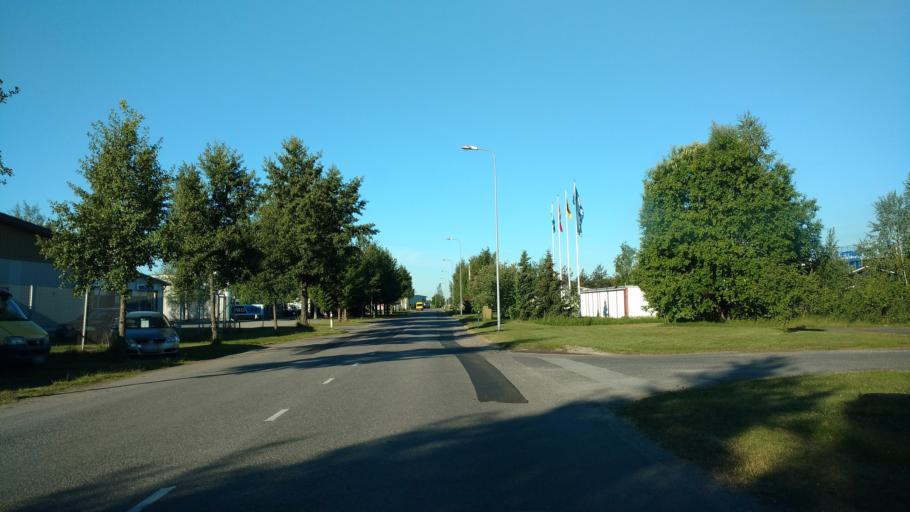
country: FI
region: Varsinais-Suomi
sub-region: Salo
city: Salo
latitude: 60.3836
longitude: 23.1075
